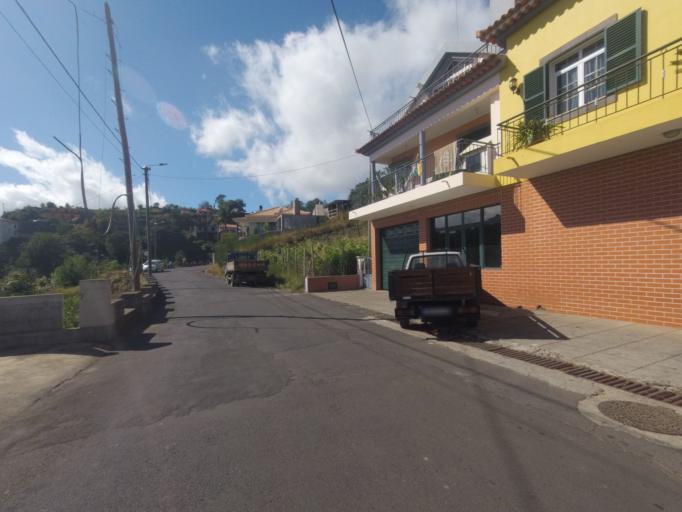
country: PT
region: Madeira
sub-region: Ribeira Brava
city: Campanario
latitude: 32.6955
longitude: -17.0172
